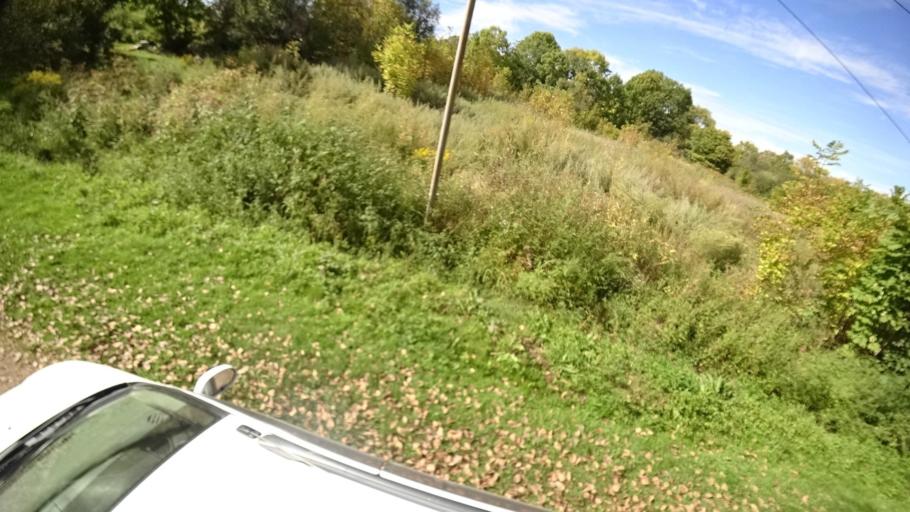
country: RU
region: Primorskiy
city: Yakovlevka
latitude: 44.3938
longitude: 133.6060
